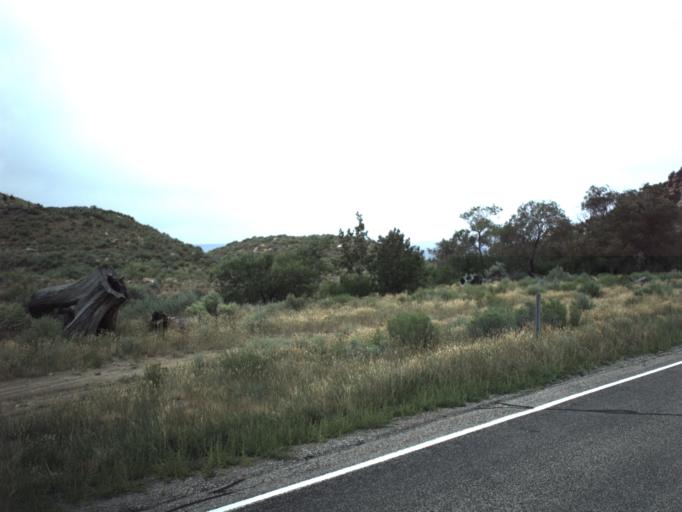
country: US
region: Utah
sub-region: Carbon County
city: East Carbon City
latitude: 39.5598
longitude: -110.3760
